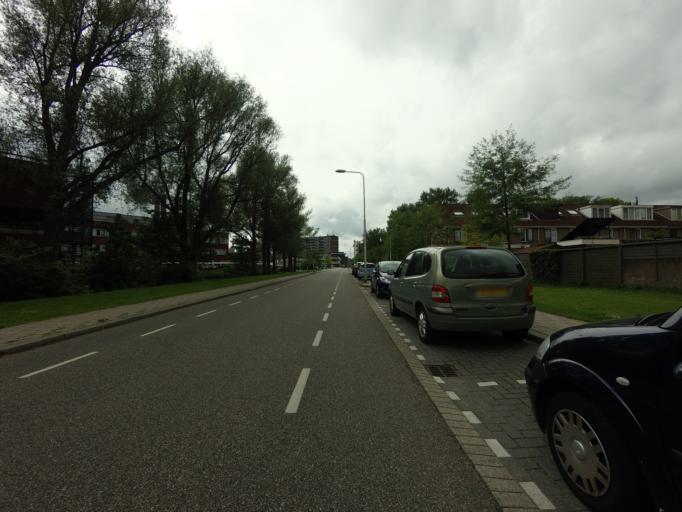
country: NL
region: South Holland
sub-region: Gemeente Gouda
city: Gouda
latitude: 52.0230
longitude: 4.7061
